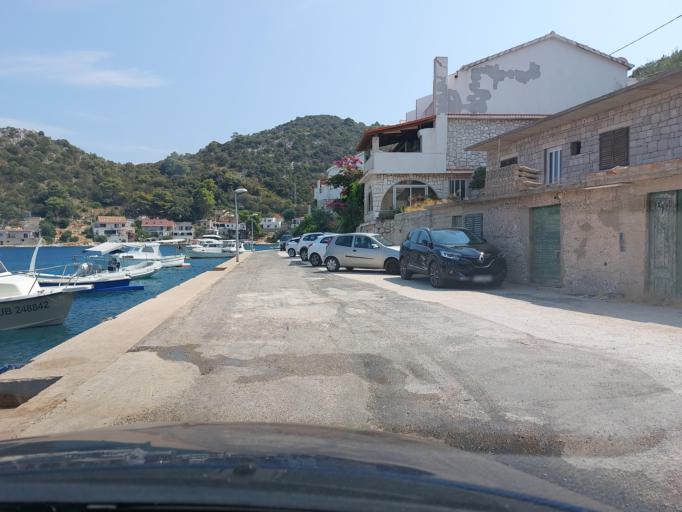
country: HR
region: Dubrovacko-Neretvanska
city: Smokvica
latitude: 42.7736
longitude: 16.8733
